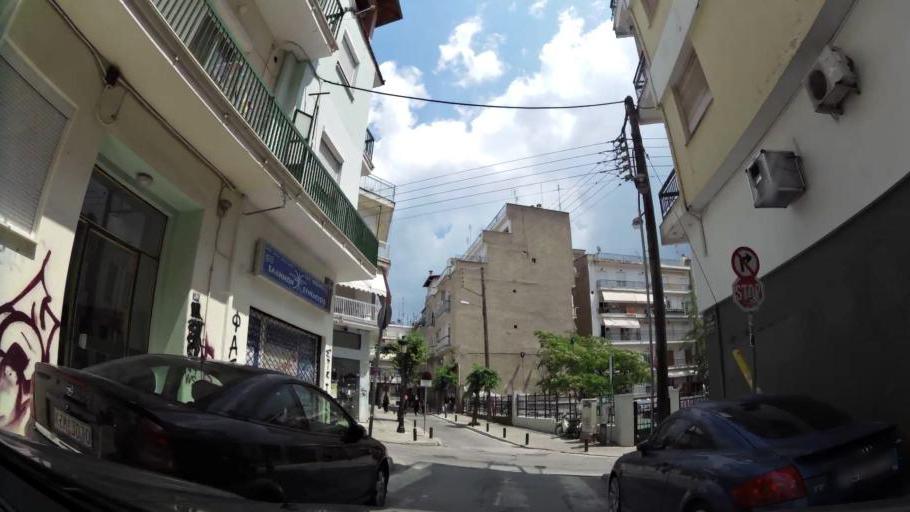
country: GR
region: West Macedonia
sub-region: Nomos Kozanis
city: Kozani
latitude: 40.3027
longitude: 21.7869
